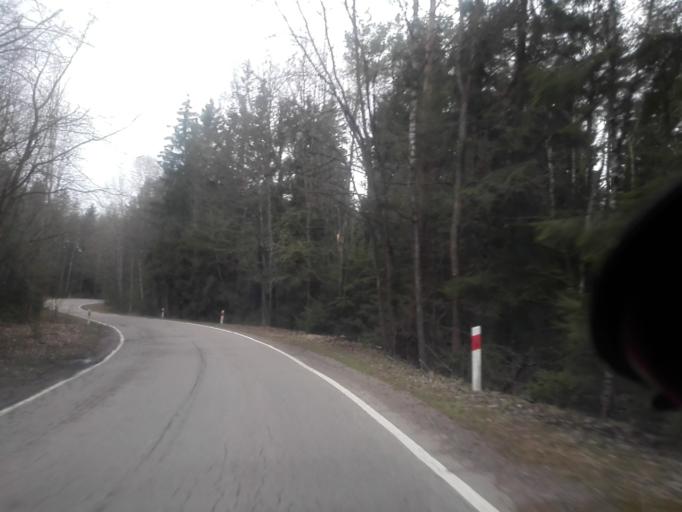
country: PL
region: Podlasie
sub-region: Powiat sejnenski
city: Krasnopol
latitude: 54.1610
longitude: 23.2375
